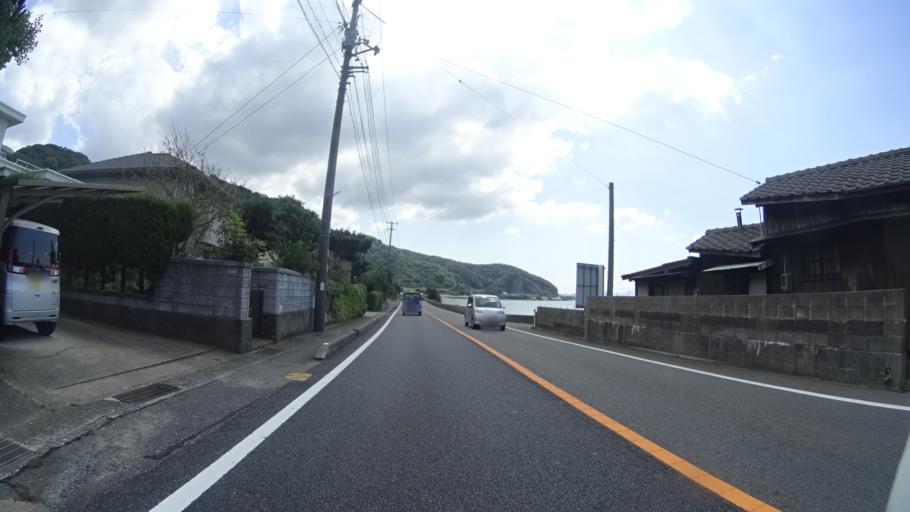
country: JP
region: Yamaguchi
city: Shimonoseki
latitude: 34.0639
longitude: 130.9081
